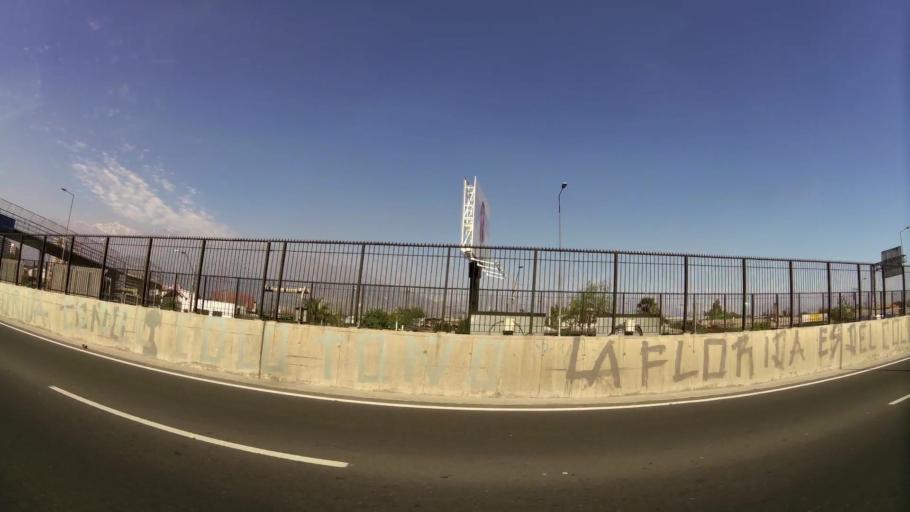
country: CL
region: Santiago Metropolitan
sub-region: Provincia de Santiago
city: La Pintana
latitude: -33.5286
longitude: -70.6041
